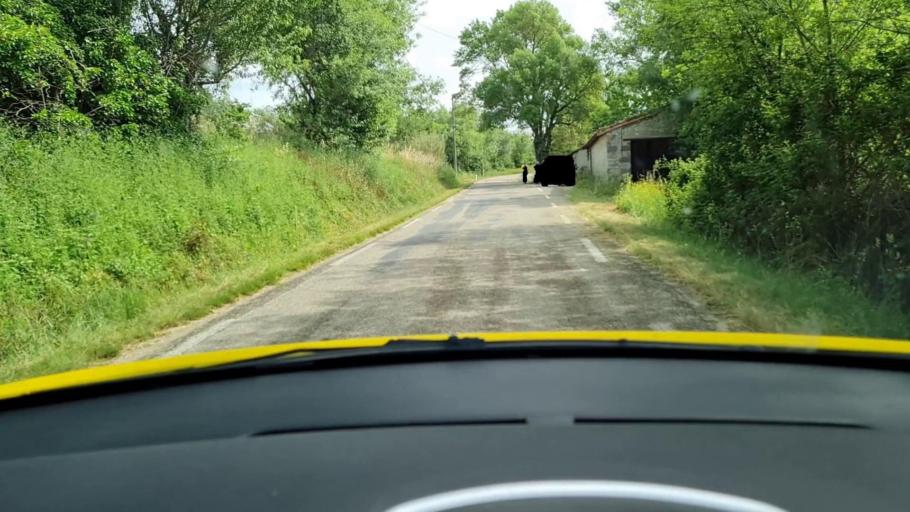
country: FR
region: Languedoc-Roussillon
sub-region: Departement du Gard
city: Quissac
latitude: 43.8444
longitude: 4.0030
